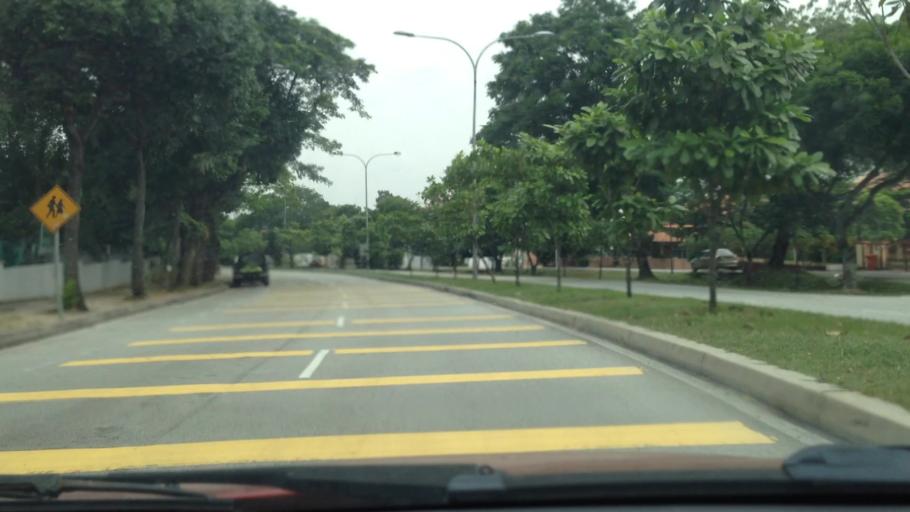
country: MY
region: Selangor
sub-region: Petaling
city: Petaling Jaya
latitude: 3.1017
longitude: 101.6076
